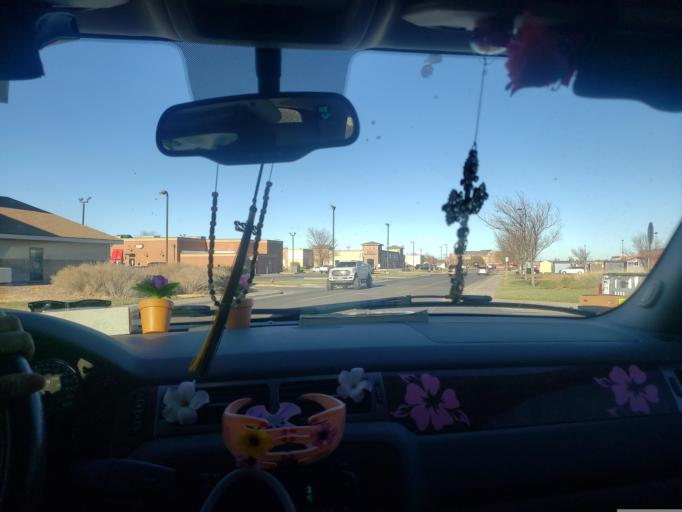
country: US
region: Kansas
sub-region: Finney County
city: Garden City
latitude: 37.9835
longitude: -100.8358
